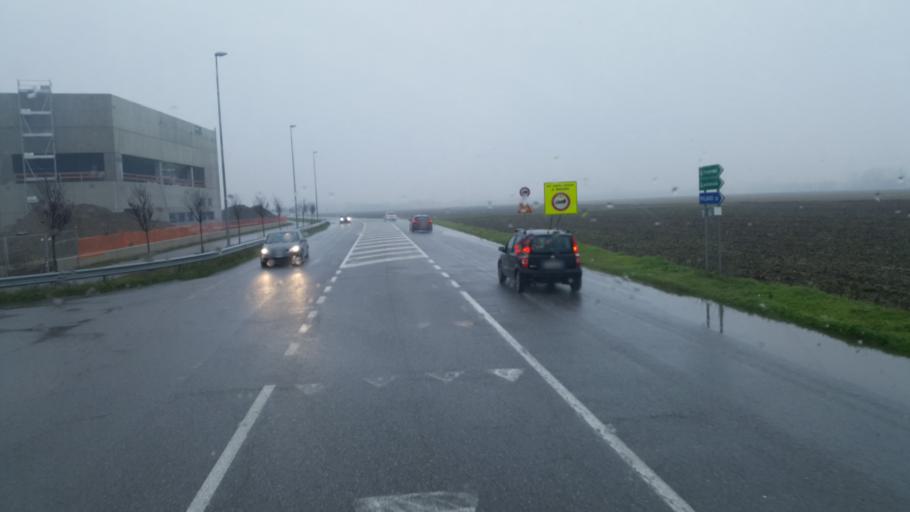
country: IT
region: Lombardy
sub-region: Provincia di Pavia
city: Marzano
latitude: 45.2614
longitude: 9.2971
